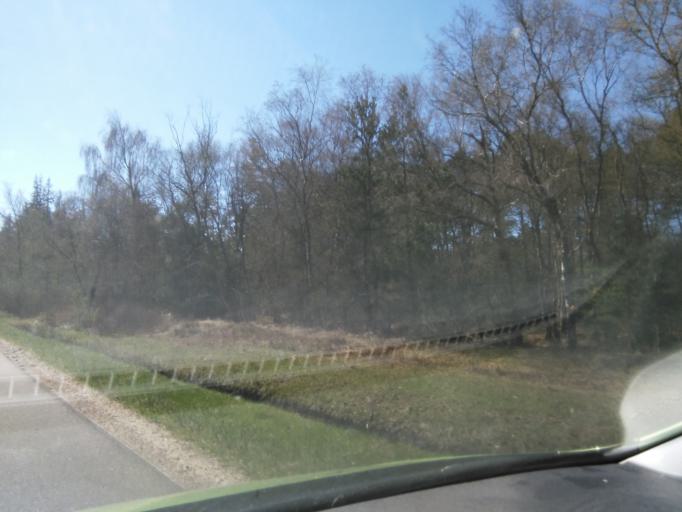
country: DK
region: South Denmark
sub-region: Varde Kommune
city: Oksbol
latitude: 55.5776
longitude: 8.2281
